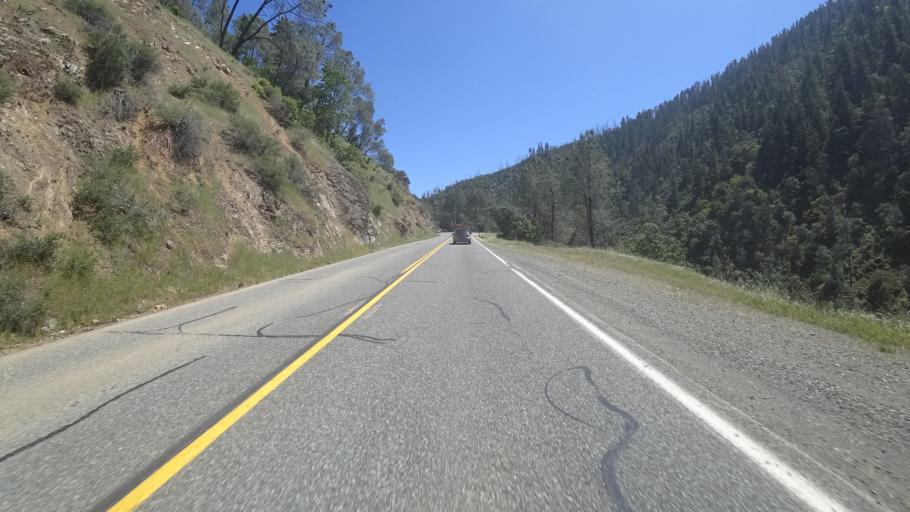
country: US
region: California
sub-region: Trinity County
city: Hayfork
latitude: 40.7948
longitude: -123.3633
